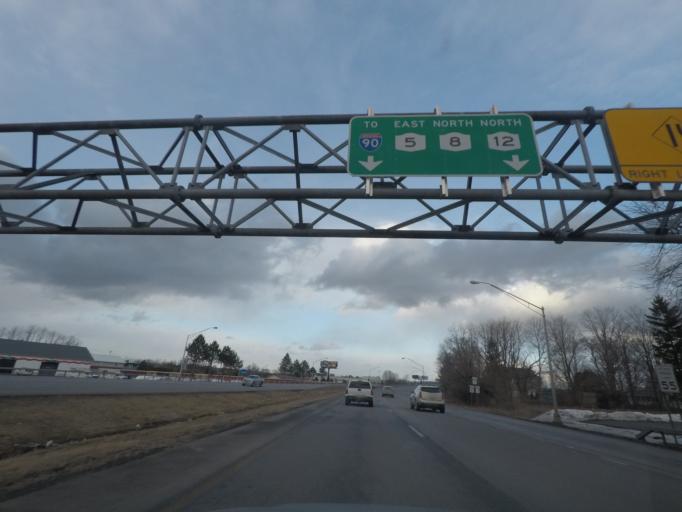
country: US
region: New York
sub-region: Oneida County
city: New Hartford
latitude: 43.0829
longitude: -75.2884
